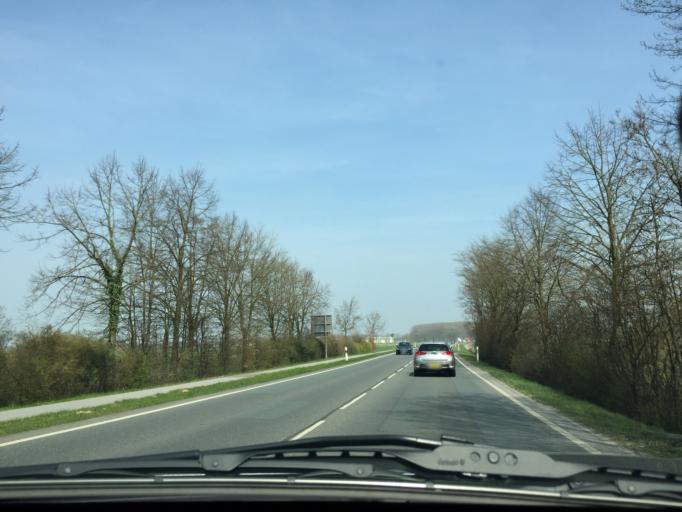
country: DE
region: North Rhine-Westphalia
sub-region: Regierungsbezirk Dusseldorf
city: Kleve
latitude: 51.7730
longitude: 6.1497
